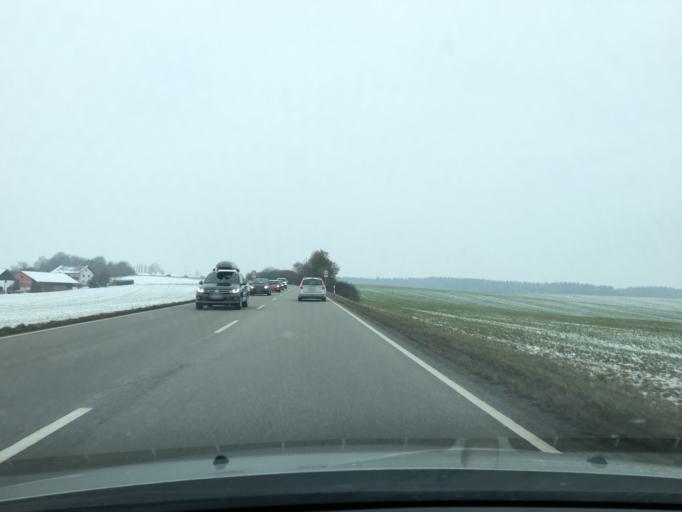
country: DE
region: Bavaria
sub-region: Lower Bavaria
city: Geisenhausen
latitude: 48.4650
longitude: 12.3053
